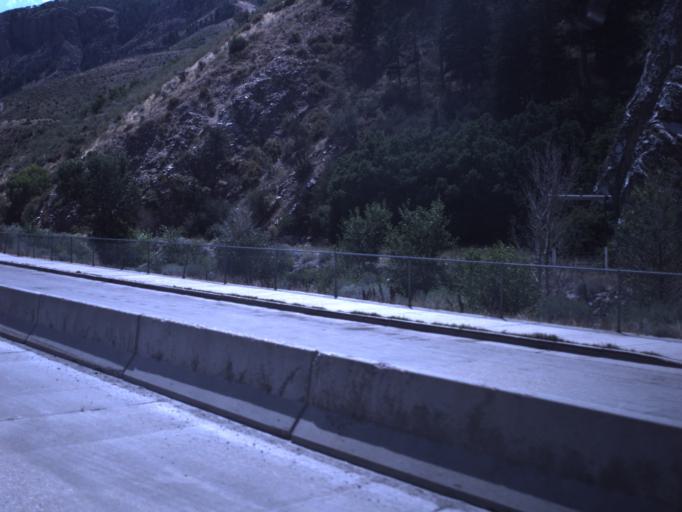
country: US
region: Utah
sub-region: Morgan County
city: Morgan
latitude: 41.0641
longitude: -111.5478
